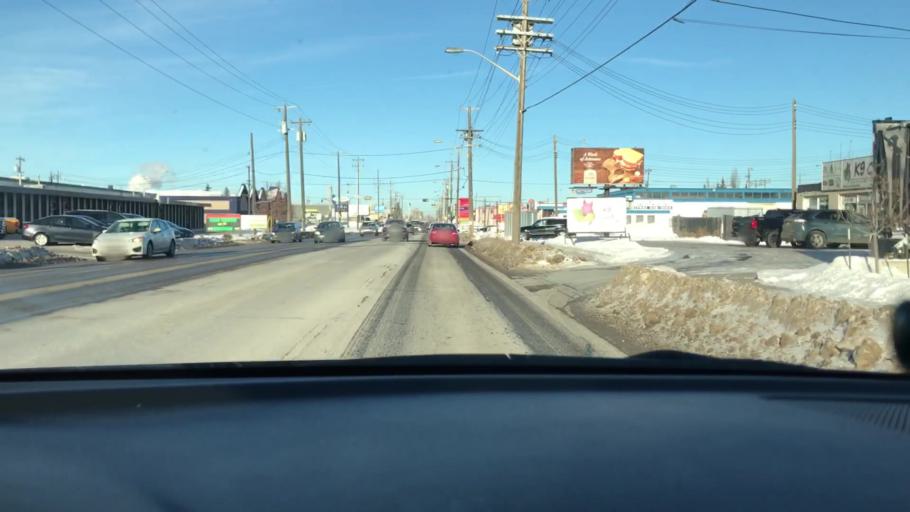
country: CA
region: Alberta
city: Edmonton
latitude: 53.4945
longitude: -113.4861
